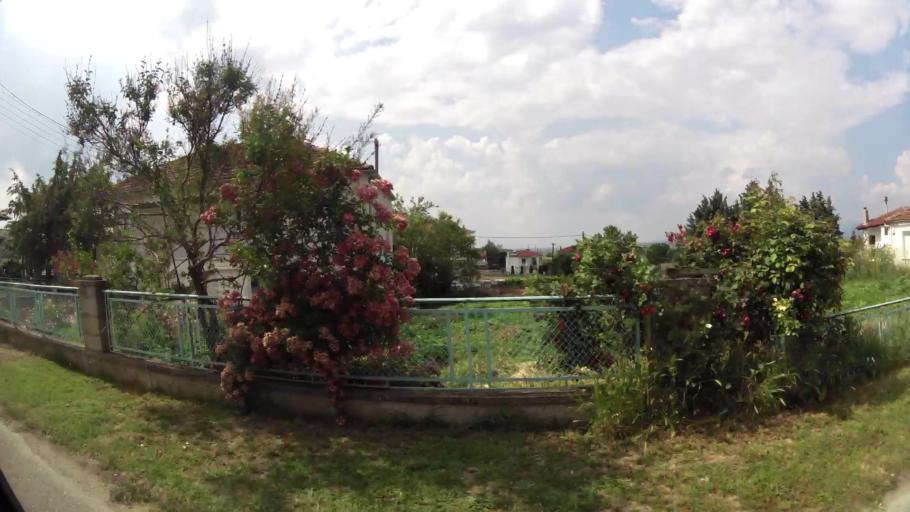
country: GR
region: West Macedonia
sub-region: Nomos Kozanis
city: Koila
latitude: 40.3511
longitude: 21.8296
